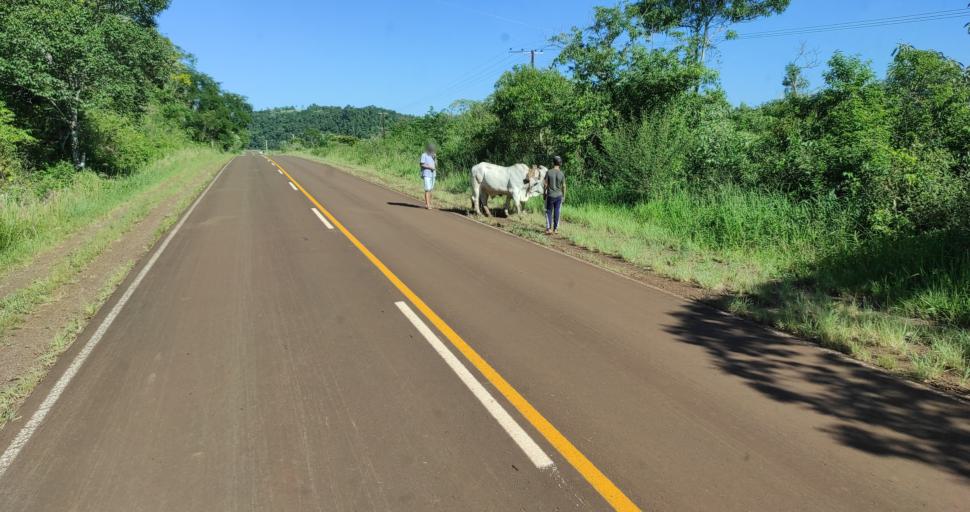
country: AR
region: Misiones
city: El Soberbio
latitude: -27.2239
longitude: -54.0654
